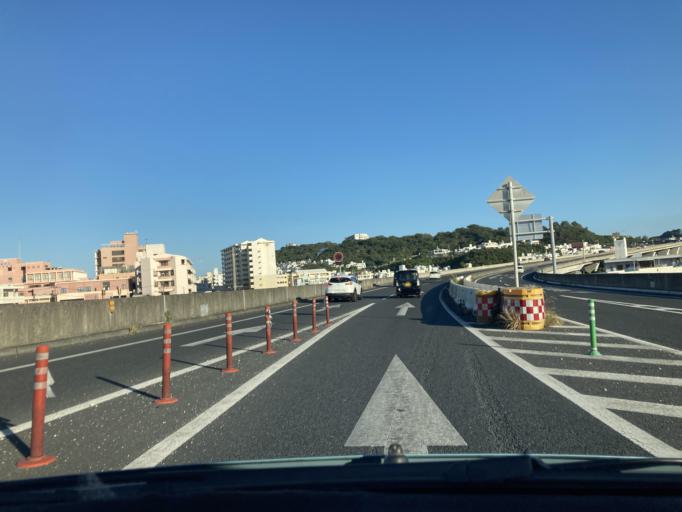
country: JP
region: Okinawa
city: Tomigusuku
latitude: 26.1755
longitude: 127.6732
